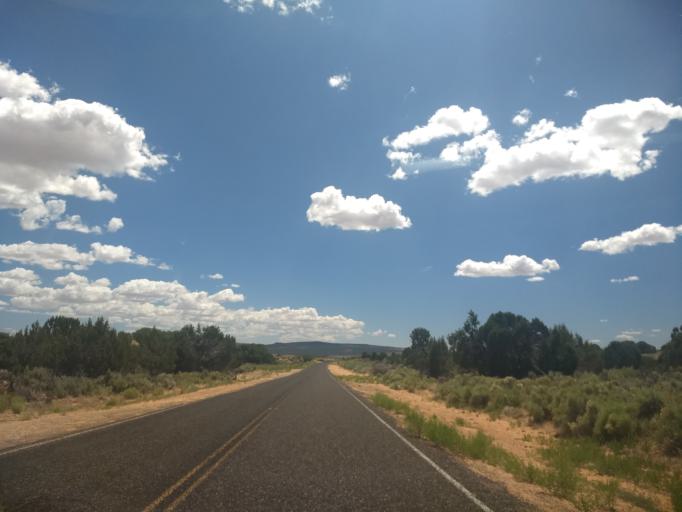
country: US
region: Utah
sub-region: Kane County
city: Kanab
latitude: 37.0453
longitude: -112.7226
